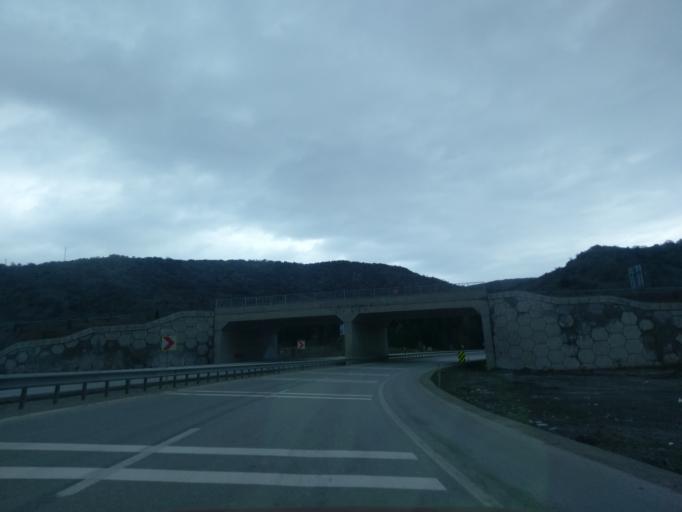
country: TR
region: Kuetahya
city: Sabuncu
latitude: 39.5758
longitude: 30.0847
